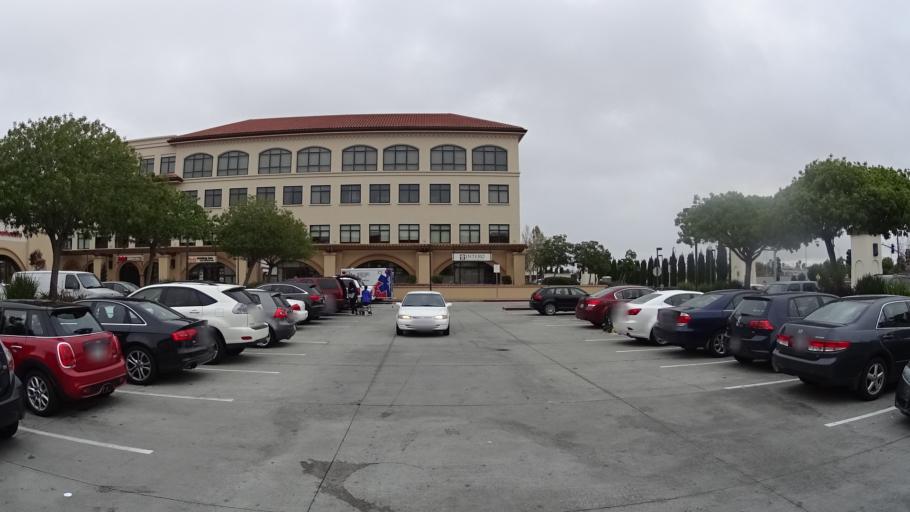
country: US
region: California
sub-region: San Mateo County
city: Foster City
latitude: 37.5443
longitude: -122.2913
